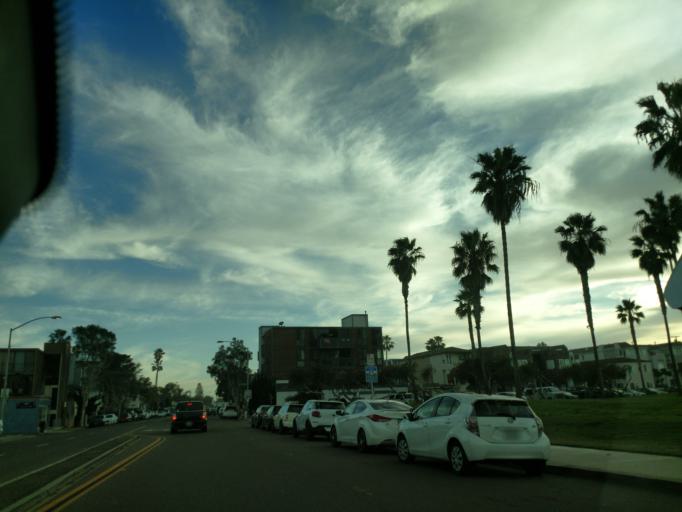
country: US
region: California
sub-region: San Diego County
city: La Jolla
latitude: 32.7683
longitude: -117.2510
